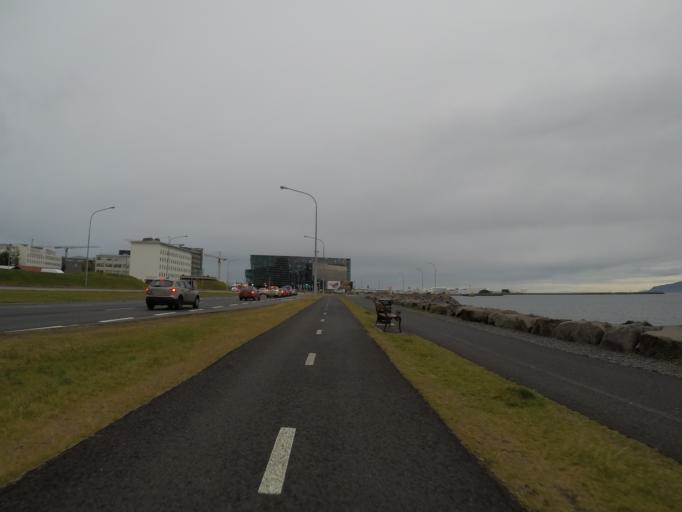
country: IS
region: Capital Region
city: Reykjavik
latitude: 64.1485
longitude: -21.9257
